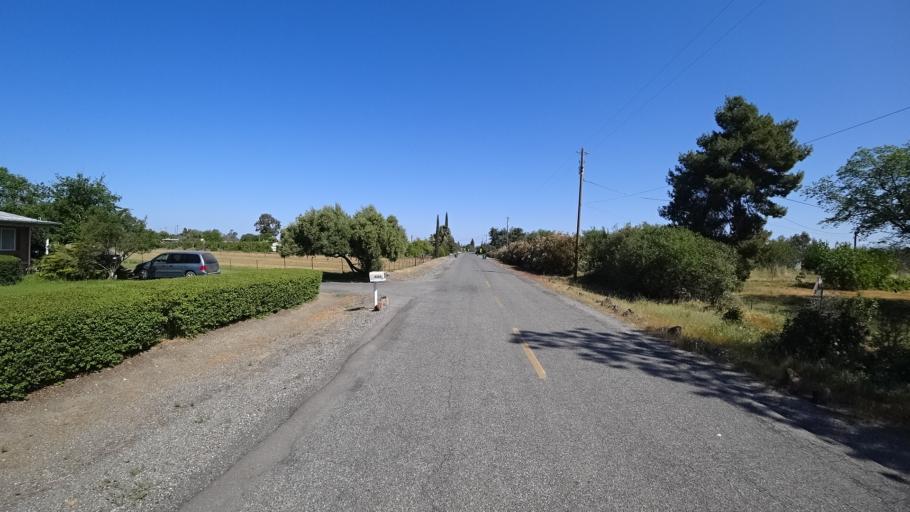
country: US
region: California
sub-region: Glenn County
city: Orland
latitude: 39.7305
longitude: -122.1923
